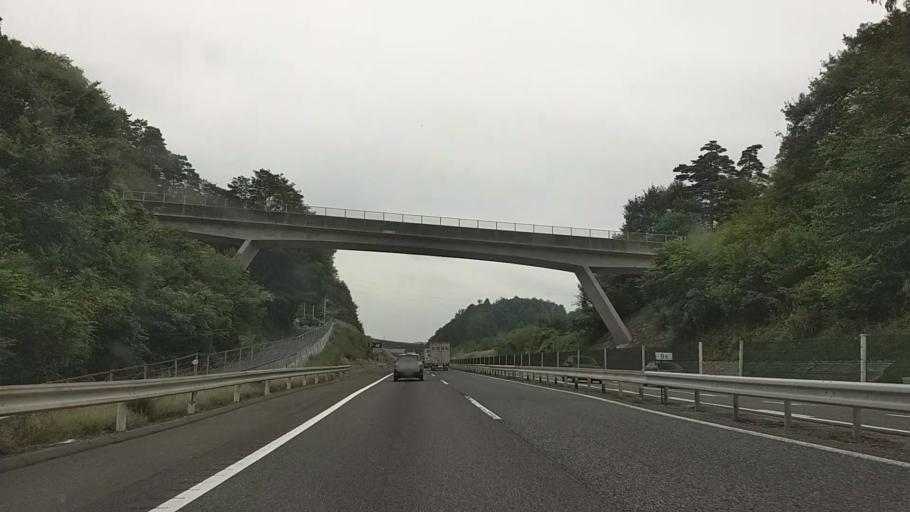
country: JP
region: Nagano
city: Shiojiri
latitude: 36.1090
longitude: 137.9879
